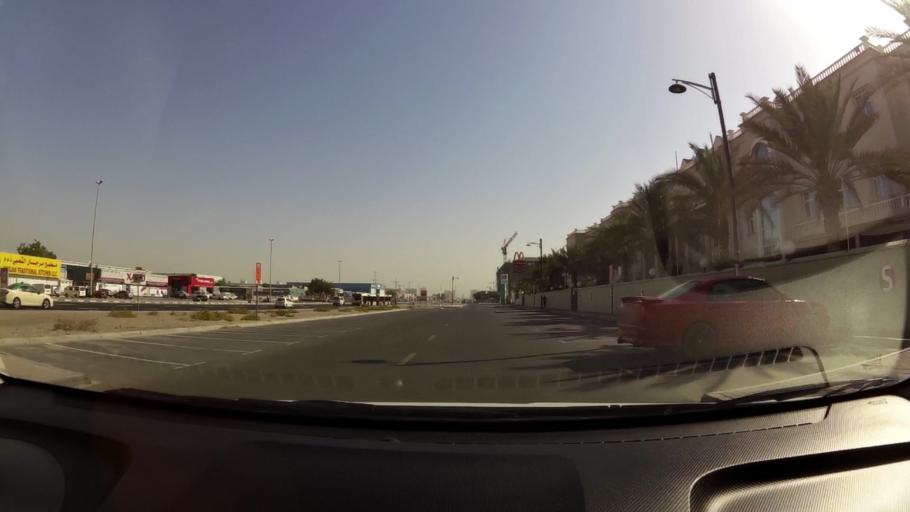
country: AE
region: Ash Shariqah
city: Sharjah
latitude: 25.2934
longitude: 55.3864
